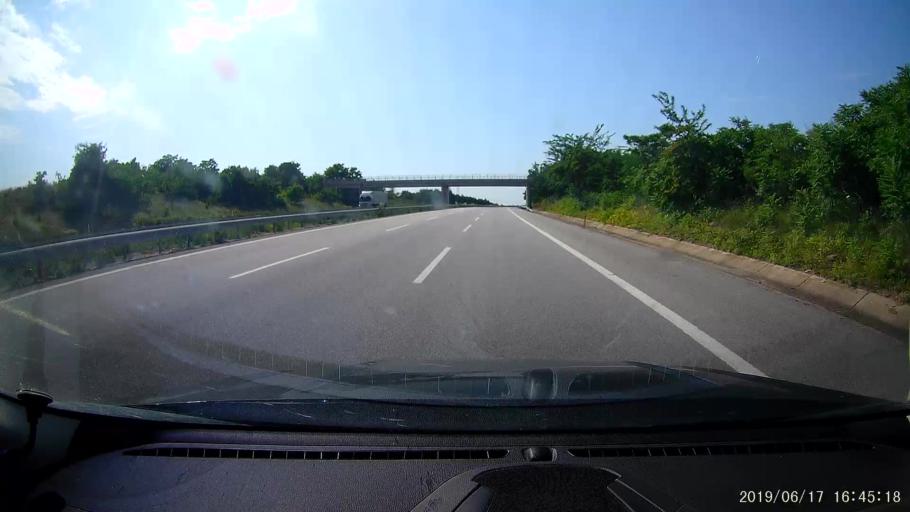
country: TR
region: Kirklareli
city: Luleburgaz
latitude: 41.4866
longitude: 27.2361
